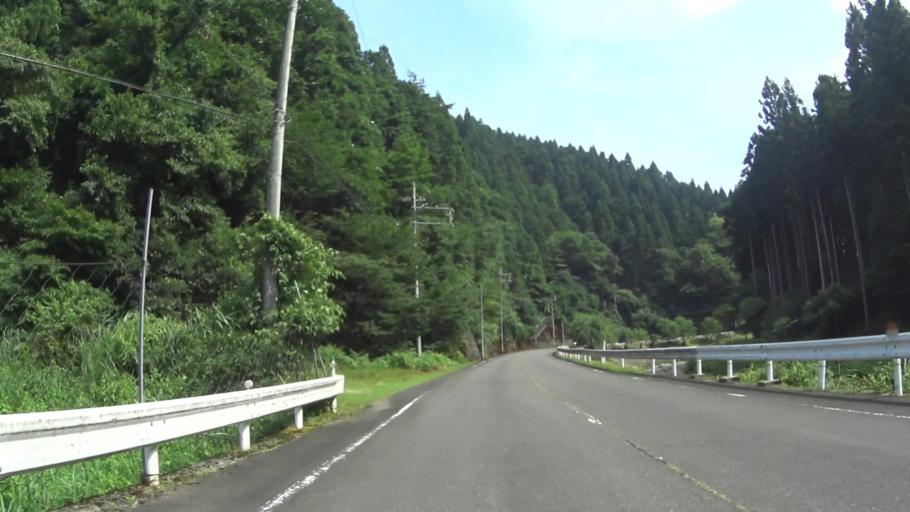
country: JP
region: Fukui
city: Obama
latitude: 35.3423
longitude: 135.6469
